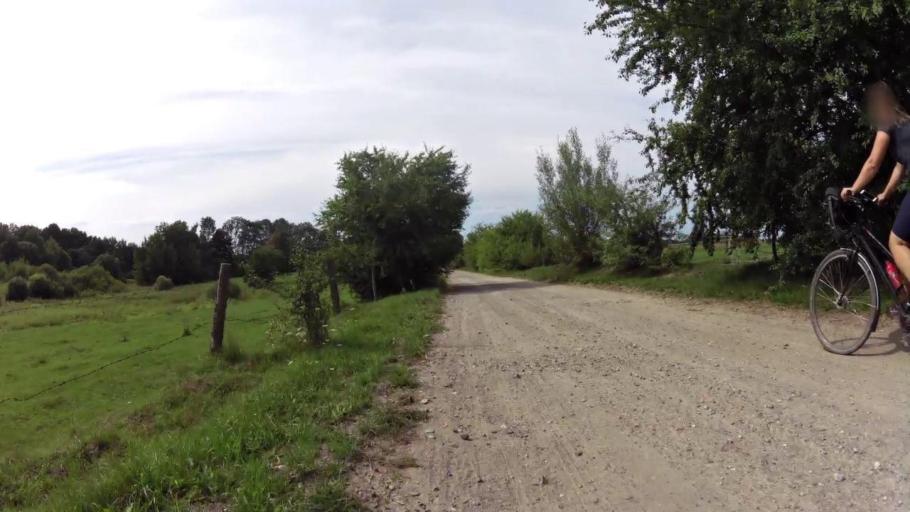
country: PL
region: West Pomeranian Voivodeship
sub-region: Powiat lobeski
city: Wegorzyno
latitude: 53.5377
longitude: 15.6075
